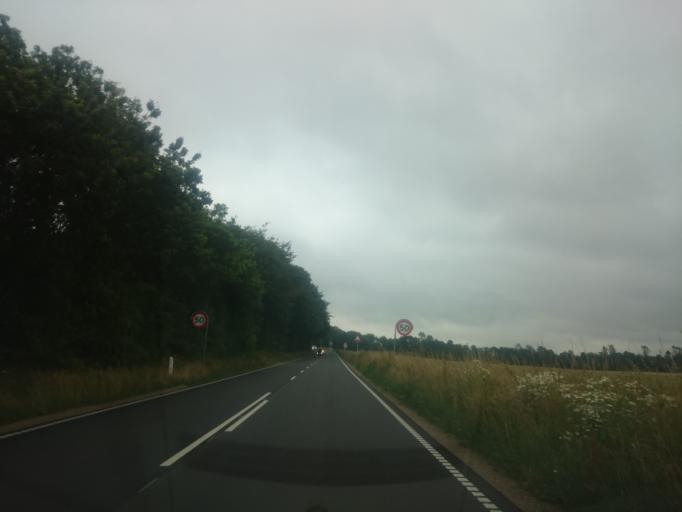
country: DK
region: South Denmark
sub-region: Billund Kommune
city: Billund
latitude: 55.7081
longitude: 9.0324
